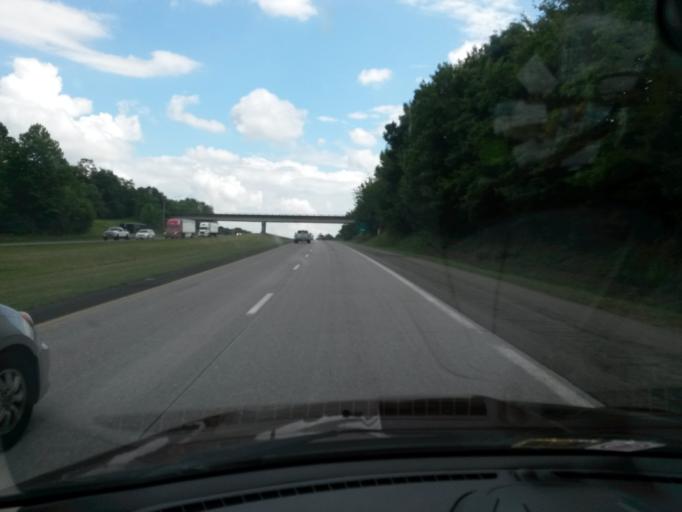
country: US
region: Virginia
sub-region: Carroll County
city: Cana
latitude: 36.5342
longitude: -80.7509
